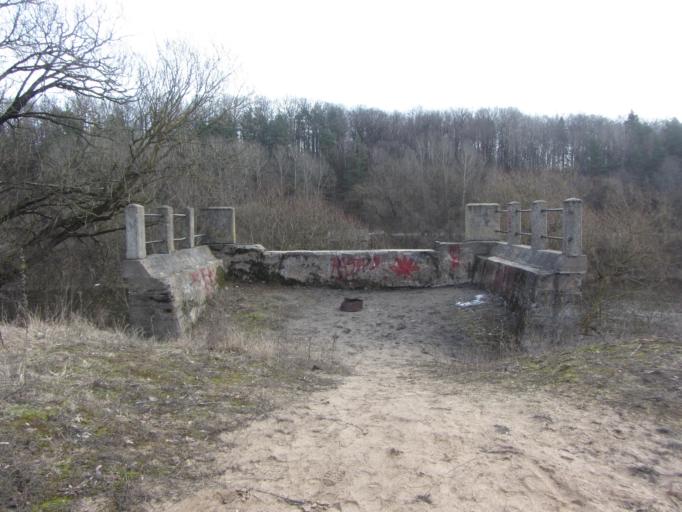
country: LT
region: Kauno apskritis
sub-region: Kauno rajonas
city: Akademija (Kaunas)
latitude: 54.9338
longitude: 23.7930
